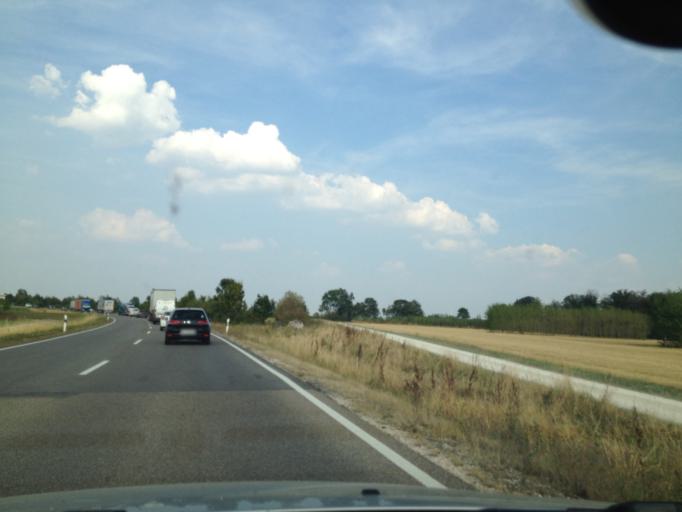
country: DE
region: Bavaria
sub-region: Swabia
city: Kaisheim
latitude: 48.7782
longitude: 10.8003
